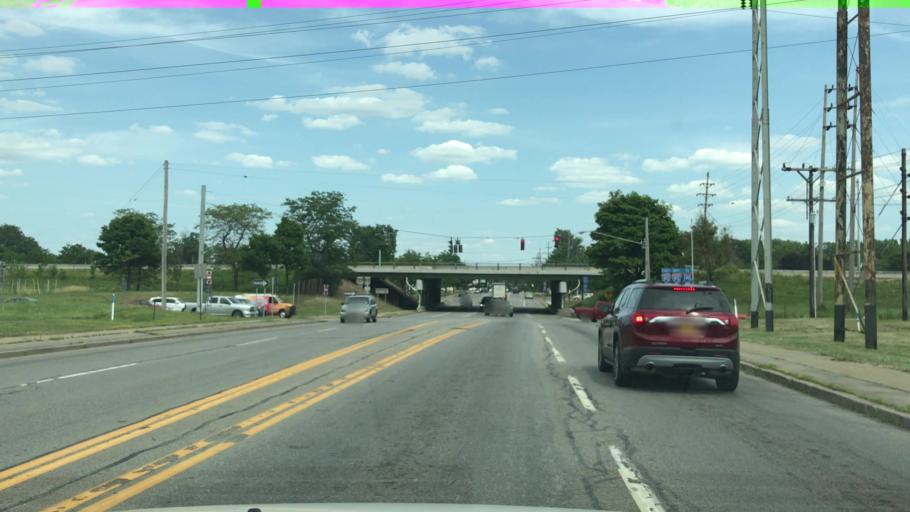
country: US
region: New York
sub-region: Erie County
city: Cheektowaga
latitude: 42.8840
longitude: -78.7699
